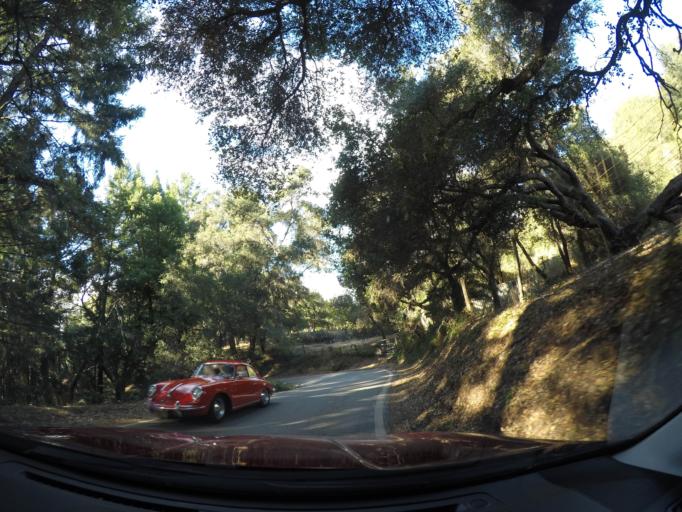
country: US
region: California
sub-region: Santa Clara County
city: Lexington Hills
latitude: 37.1596
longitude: -122.0078
